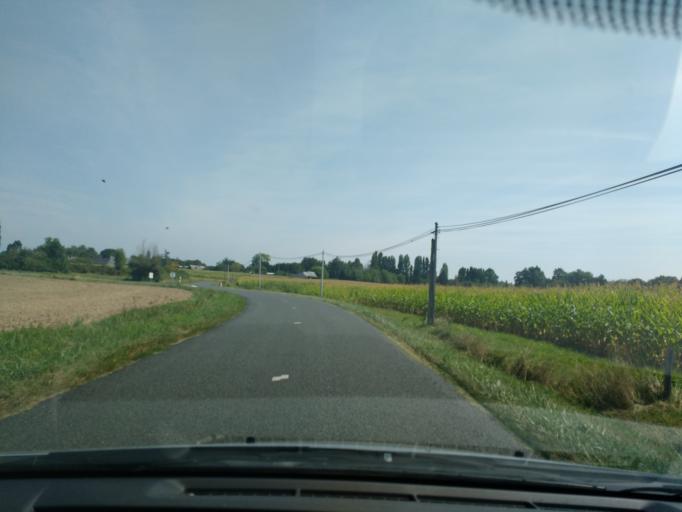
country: FR
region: Pays de la Loire
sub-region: Departement de Maine-et-Loire
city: Maze
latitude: 47.4748
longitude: -0.2526
